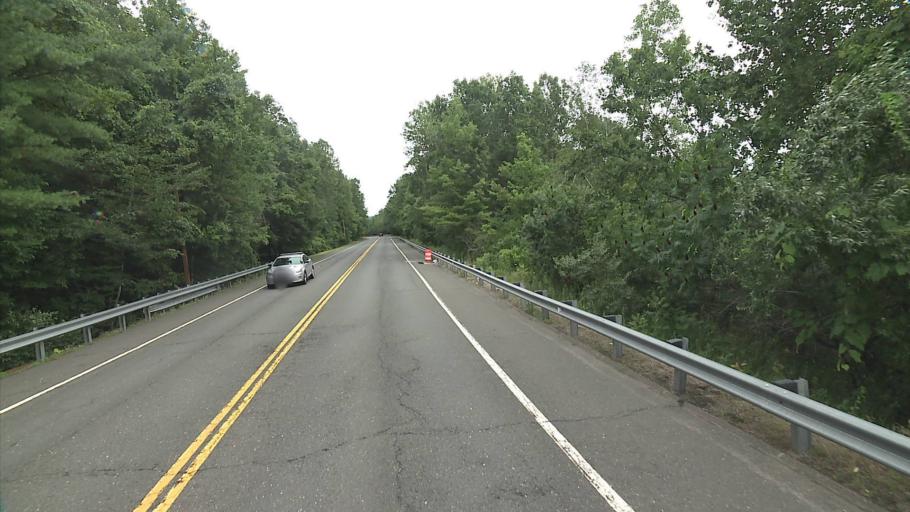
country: US
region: Connecticut
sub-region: Litchfield County
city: Winsted
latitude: 42.0004
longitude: -73.0473
